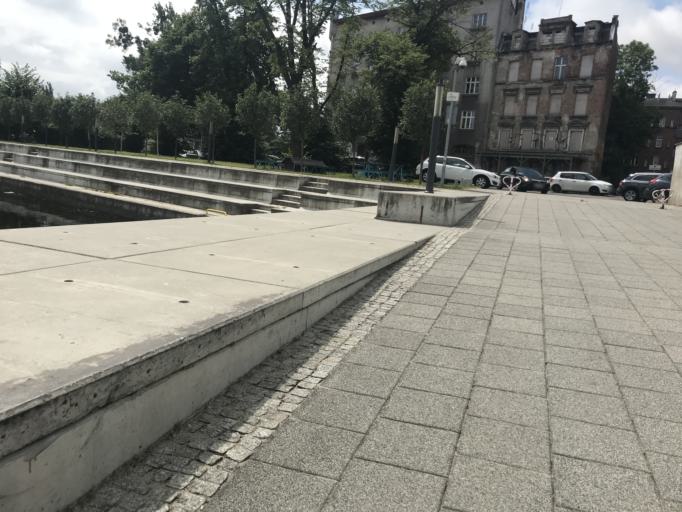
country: PL
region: Pomeranian Voivodeship
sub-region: Gdansk
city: Gdansk
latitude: 54.3420
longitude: 18.6487
